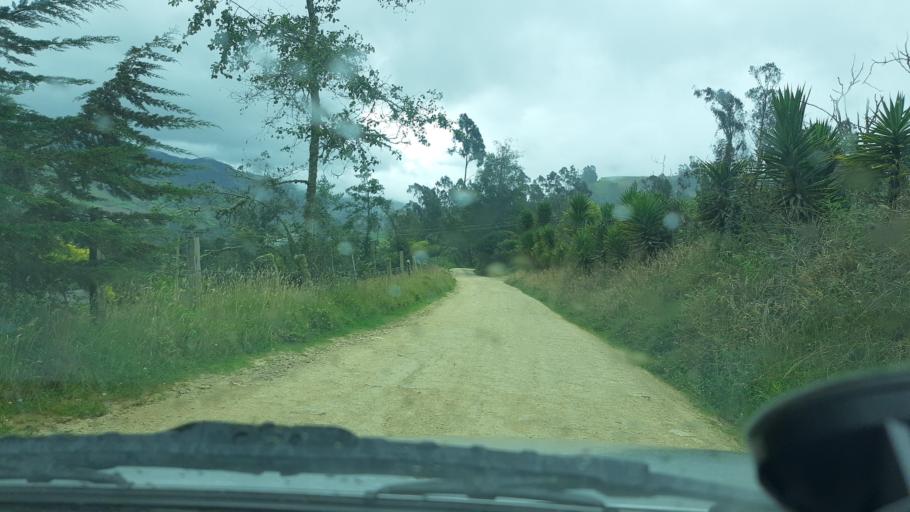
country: CO
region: Cundinamarca
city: Umbita
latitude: 5.2483
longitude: -73.4663
